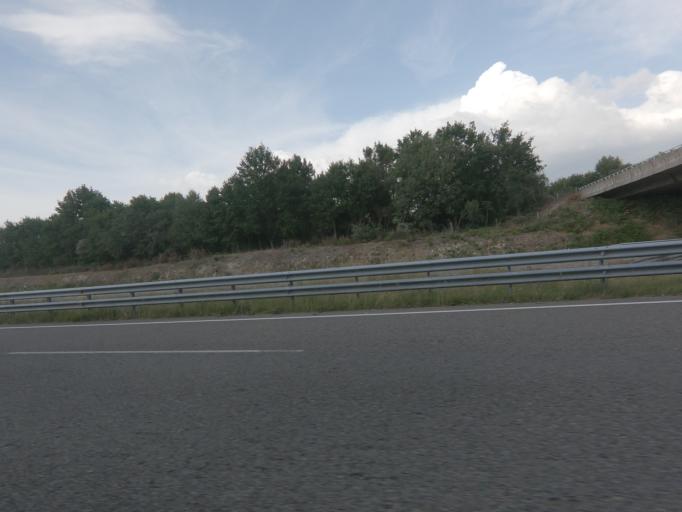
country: ES
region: Galicia
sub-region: Provincia de Ourense
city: Ambia
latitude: 42.1504
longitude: -7.7539
